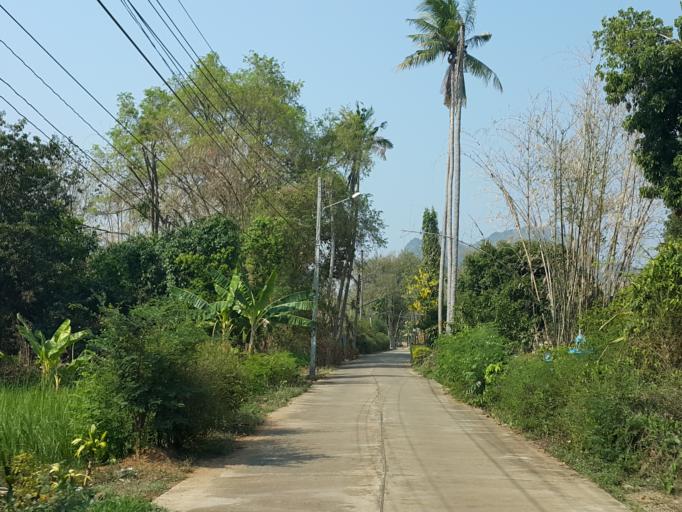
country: TH
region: Kanchanaburi
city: Sai Yok
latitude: 14.1151
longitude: 99.1365
